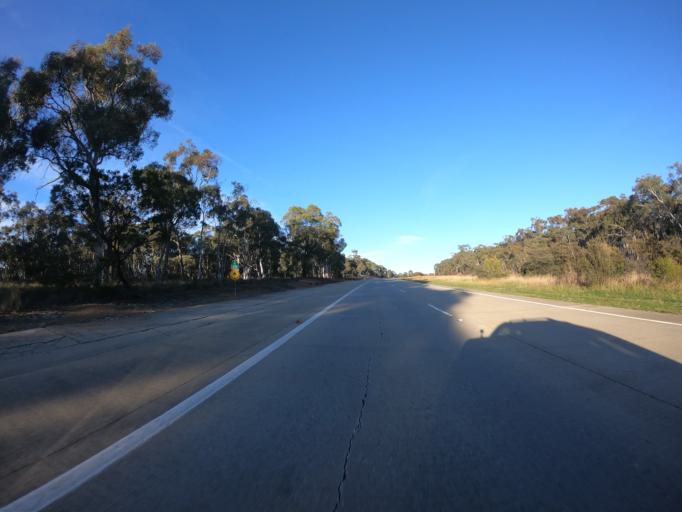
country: AU
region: New South Wales
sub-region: Yass Valley
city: Gundaroo
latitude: -35.1568
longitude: 149.3259
